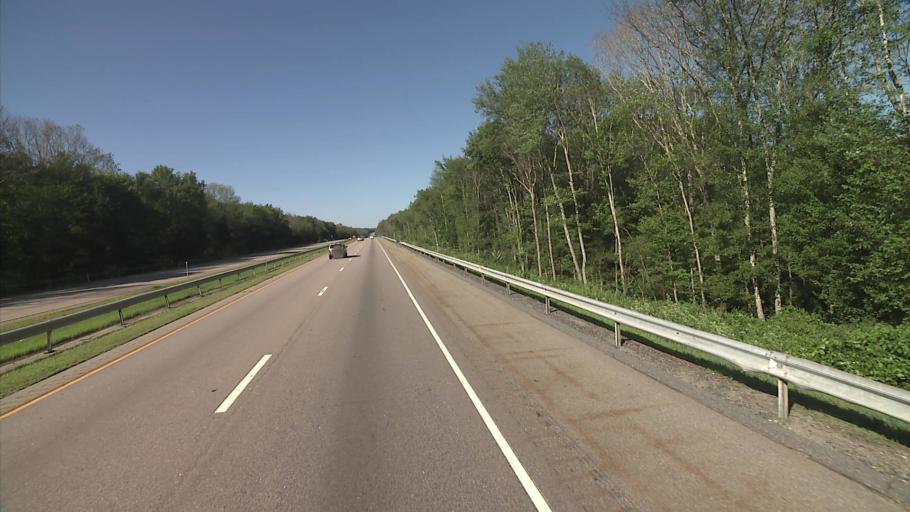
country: US
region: Connecticut
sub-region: New London County
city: Oxoboxo River
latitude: 41.4225
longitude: -72.1300
